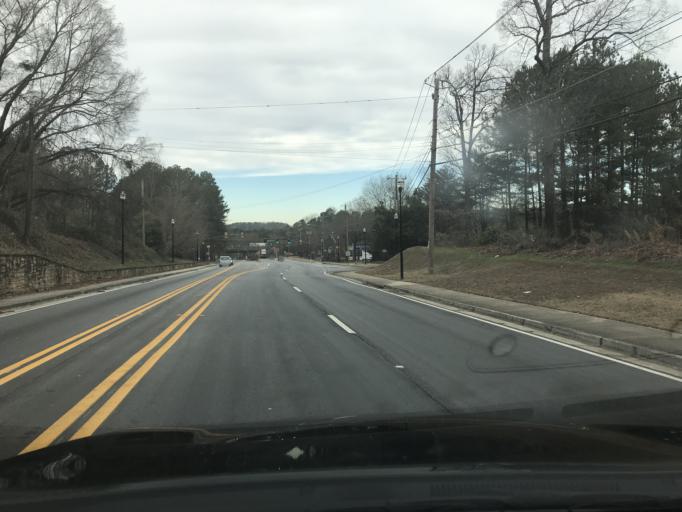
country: US
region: Georgia
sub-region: Fulton County
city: East Point
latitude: 33.7221
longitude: -84.4979
